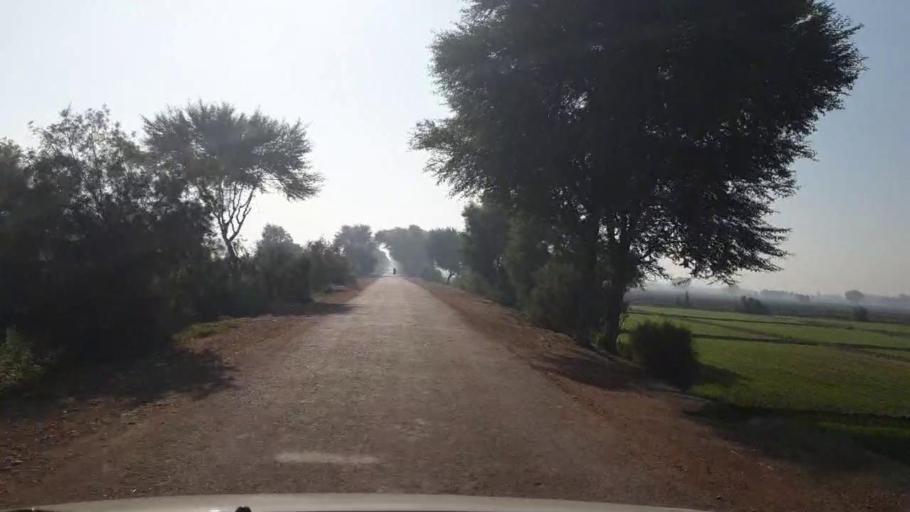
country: PK
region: Sindh
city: Dadu
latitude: 26.6649
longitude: 67.8175
